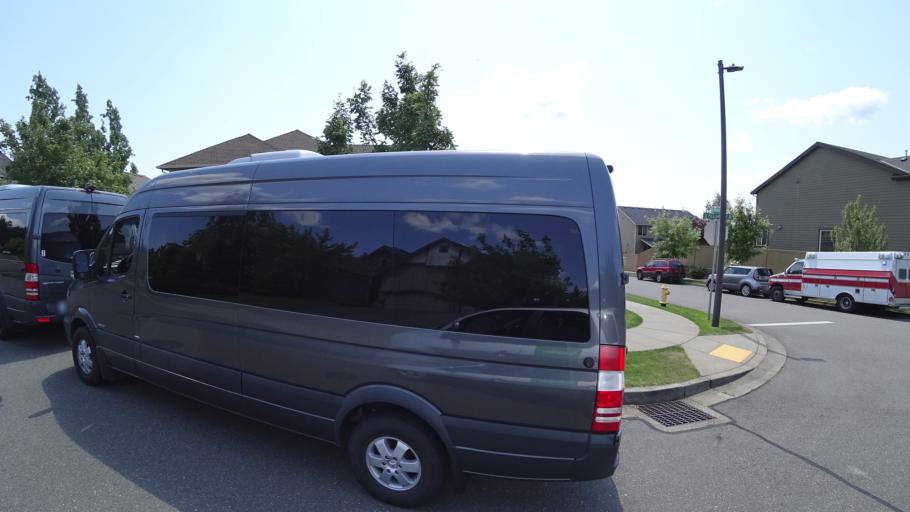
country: US
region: Oregon
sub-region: Clackamas County
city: Happy Valley
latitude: 45.4464
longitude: -122.5486
